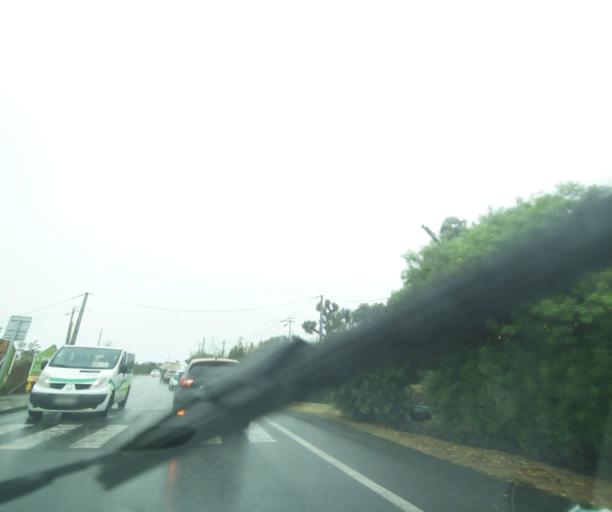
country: RE
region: Reunion
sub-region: Reunion
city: Saint-Paul
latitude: -21.0353
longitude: 55.2724
